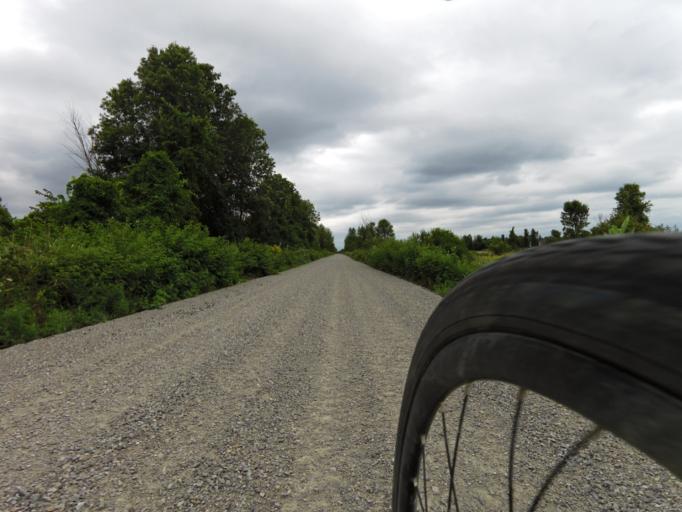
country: CA
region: Ontario
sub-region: Lanark County
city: Smiths Falls
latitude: 44.9340
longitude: -76.0359
